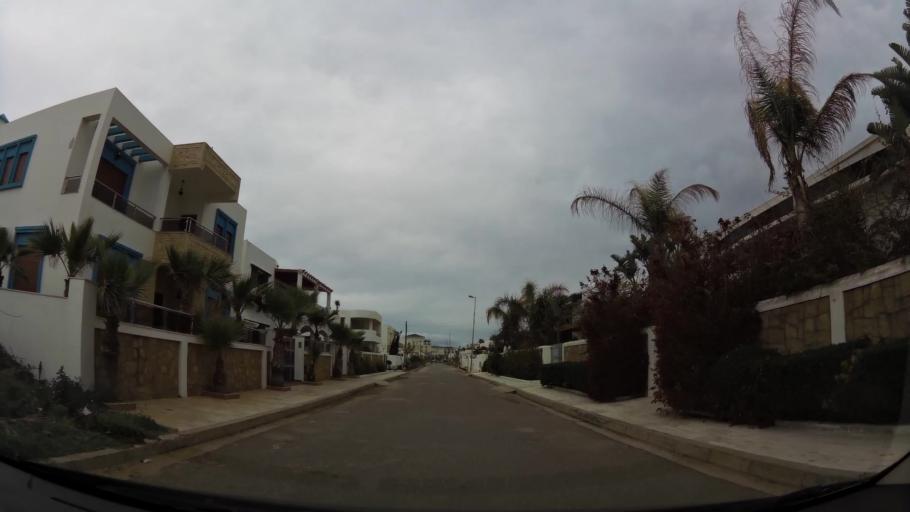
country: MA
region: Tanger-Tetouan
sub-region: Tetouan
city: Martil
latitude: 35.7421
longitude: -5.3418
